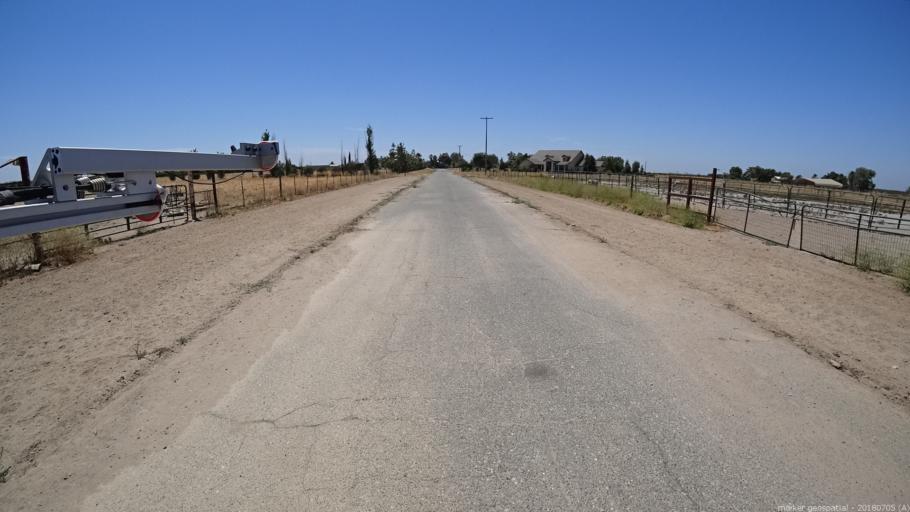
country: US
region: California
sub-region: Madera County
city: Madera Acres
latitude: 37.0967
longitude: -120.1028
